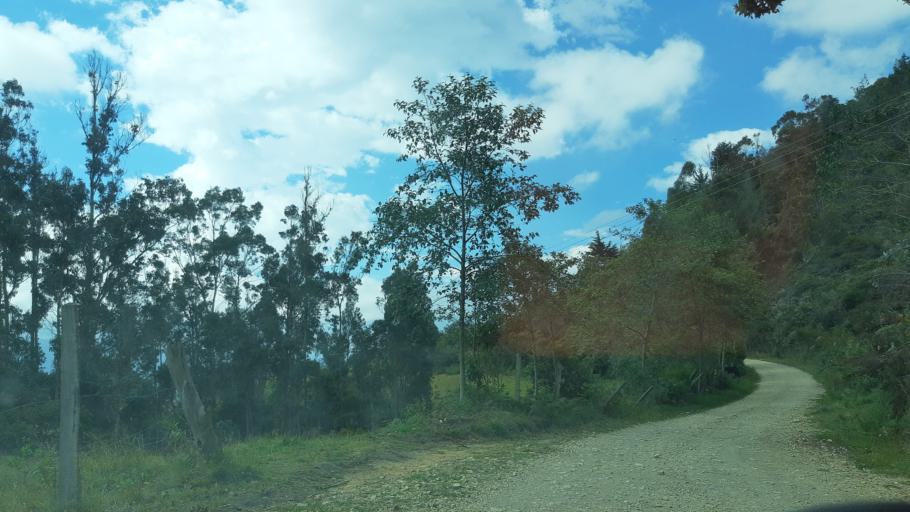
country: CO
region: Boyaca
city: Santa Sofia
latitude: 5.7267
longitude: -73.5525
